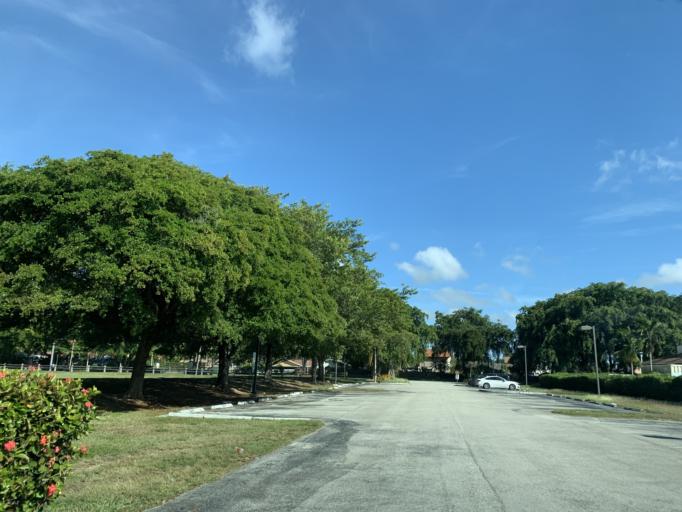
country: US
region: Florida
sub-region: Miami-Dade County
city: The Hammocks
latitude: 25.6801
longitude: -80.4361
